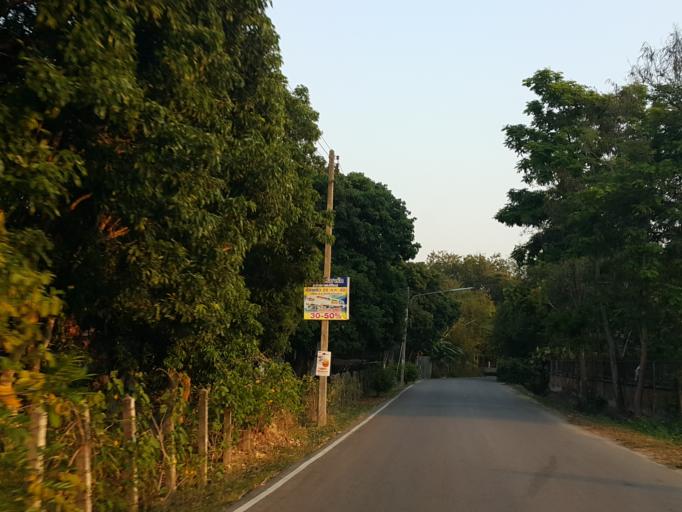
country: TH
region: Chiang Mai
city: San Sai
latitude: 18.8877
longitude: 98.9661
